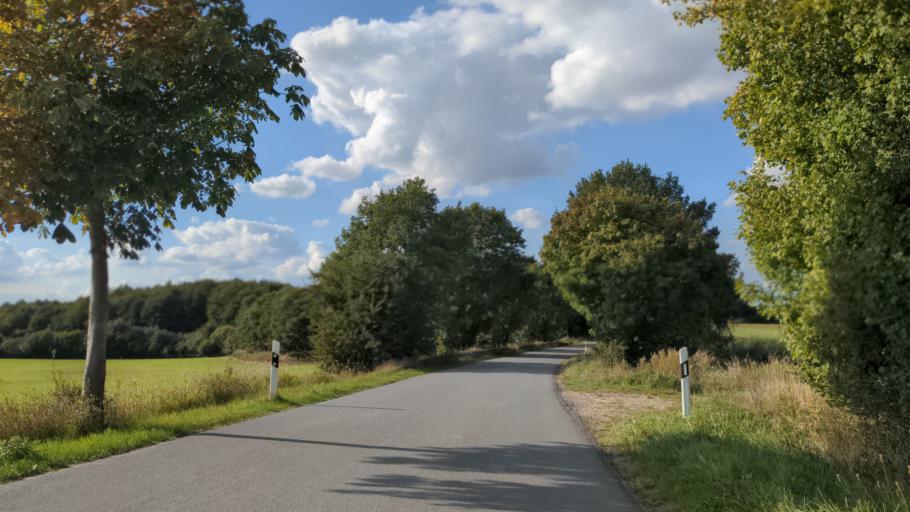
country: DE
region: Schleswig-Holstein
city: Monkhagen
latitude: 53.9189
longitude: 10.5868
